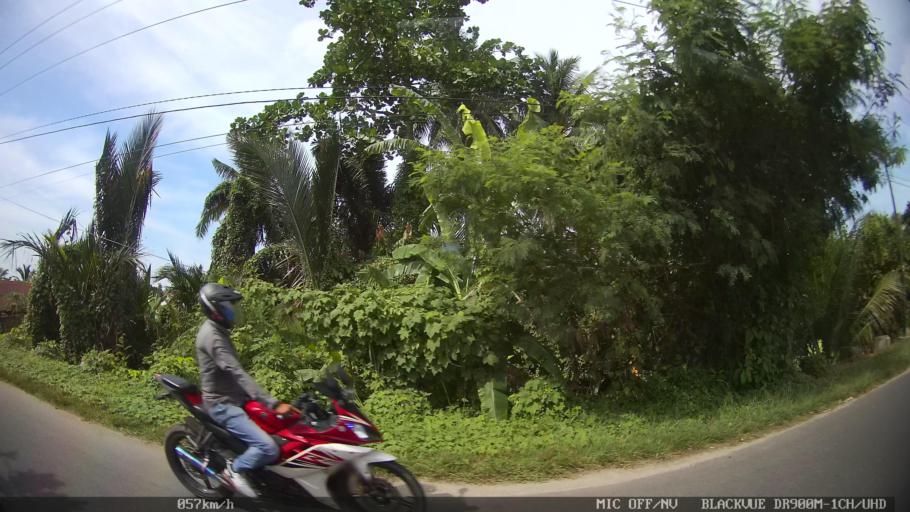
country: ID
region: North Sumatra
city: Percut
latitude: 3.6126
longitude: 98.8450
